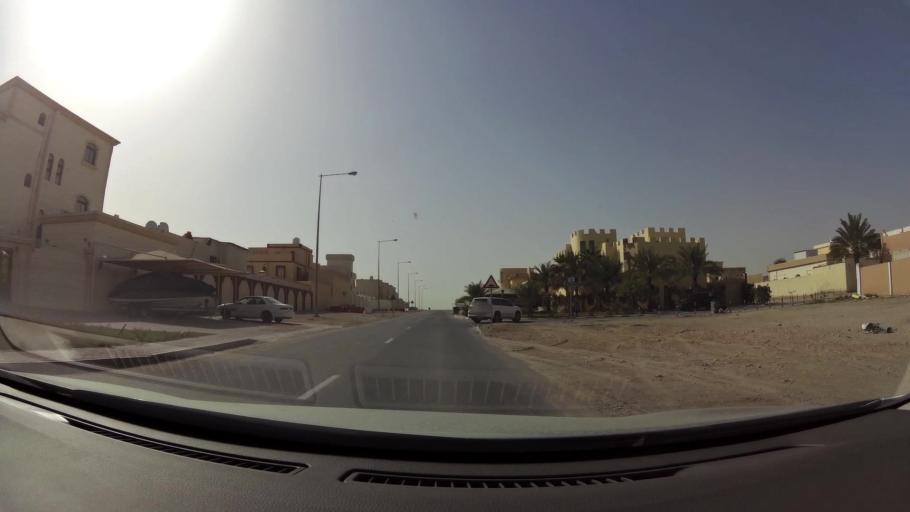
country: QA
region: Baladiyat ar Rayyan
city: Ar Rayyan
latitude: 25.3412
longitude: 51.4220
